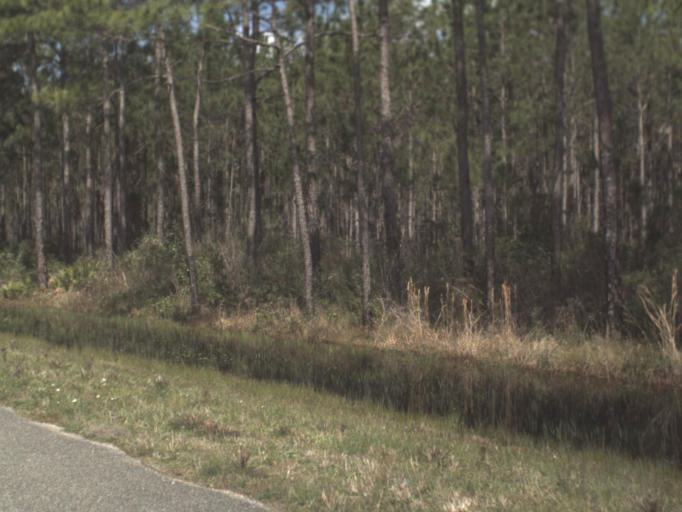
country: US
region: Florida
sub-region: Franklin County
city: Apalachicola
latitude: 29.7302
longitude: -85.1385
